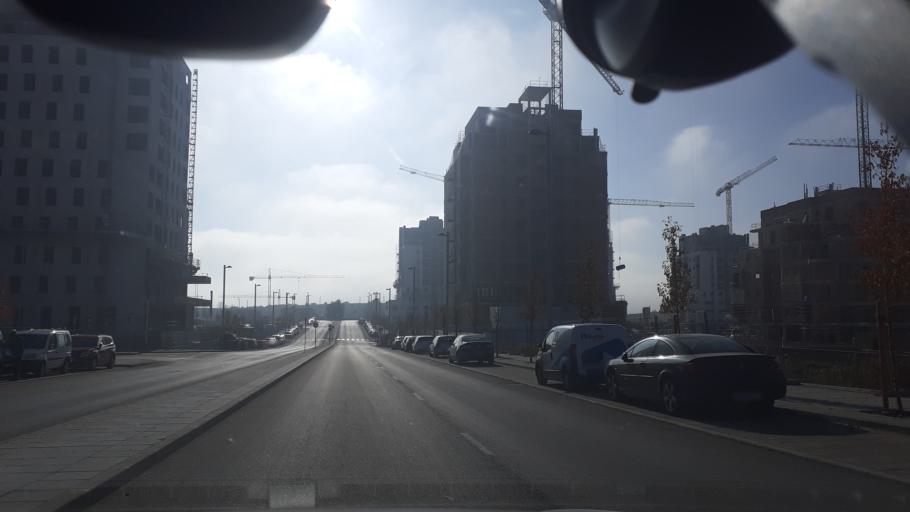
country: ES
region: Madrid
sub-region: Provincia de Madrid
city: Coslada
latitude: 40.4013
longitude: -3.5568
